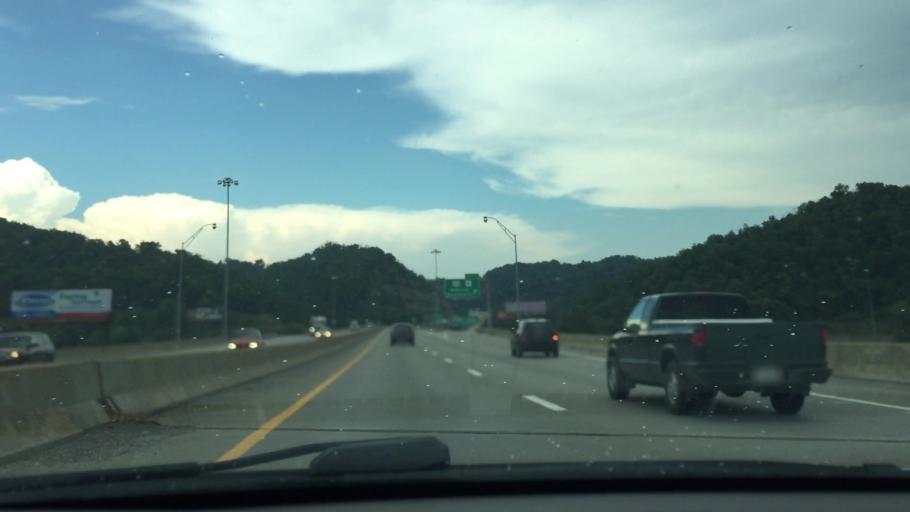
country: US
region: West Virginia
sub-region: Ohio County
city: Wheeling
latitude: 40.0503
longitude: -80.7272
